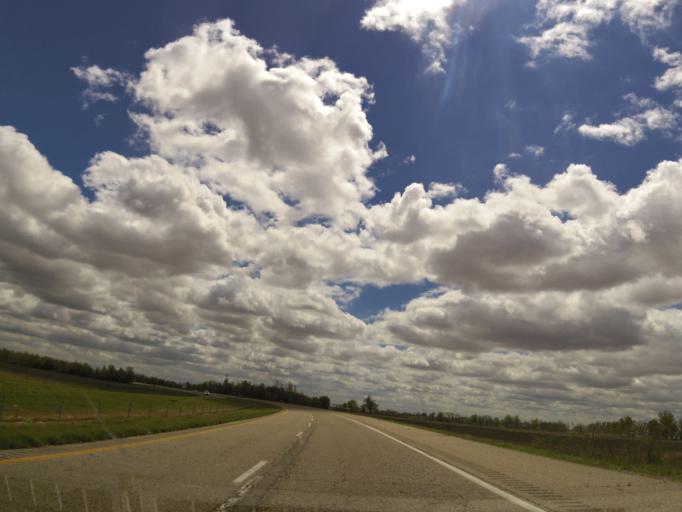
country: US
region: Arkansas
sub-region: Poinsett County
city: Trumann
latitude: 35.6643
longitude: -90.5513
